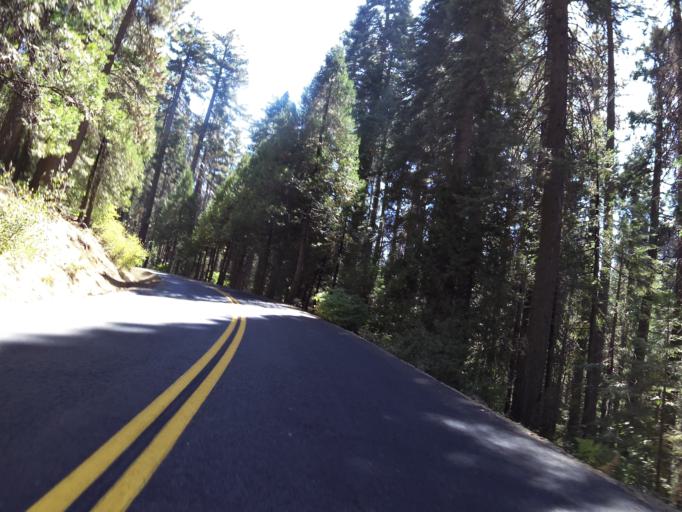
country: US
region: California
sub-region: Madera County
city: Oakhurst
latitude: 37.4147
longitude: -119.5776
